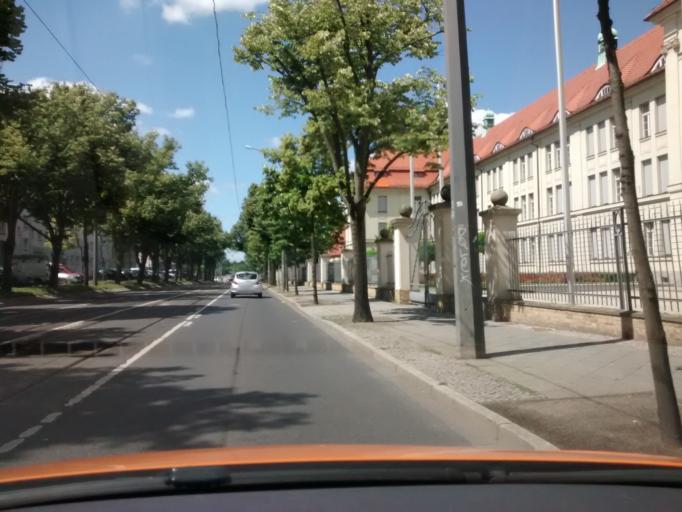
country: DE
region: Brandenburg
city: Potsdam
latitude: 52.3878
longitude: 13.0689
